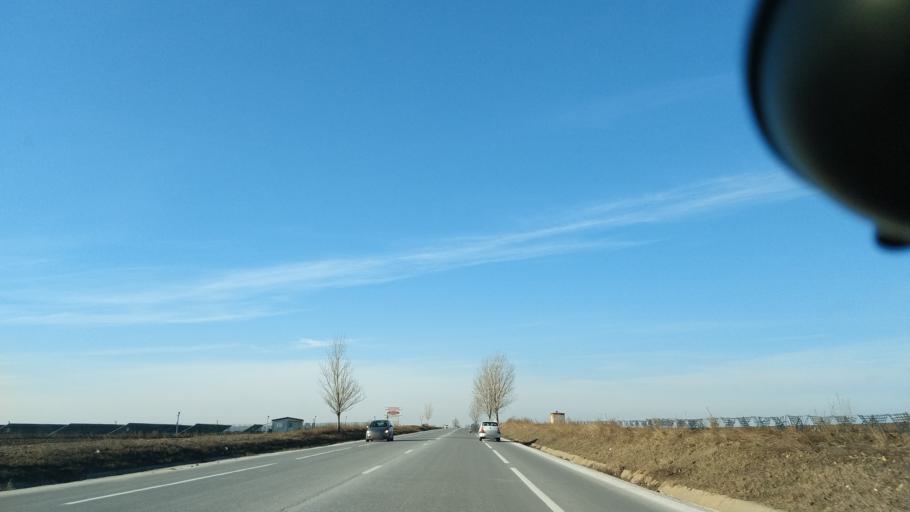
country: RO
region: Iasi
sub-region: Comuna Podu Iloaiei
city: Budai
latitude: 47.2224
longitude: 27.1972
